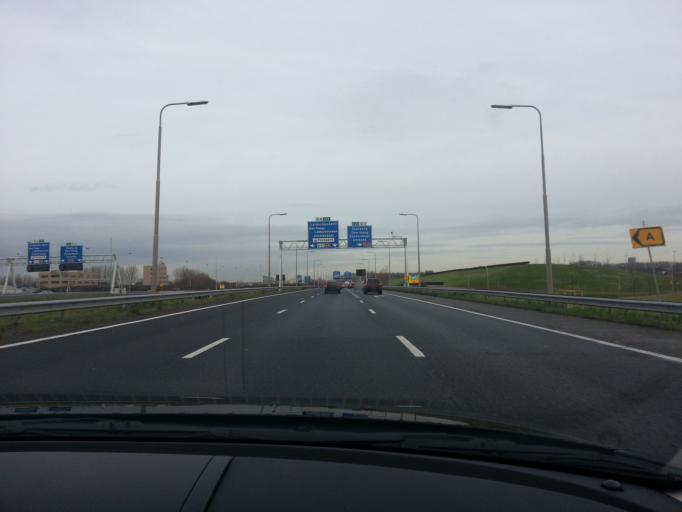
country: NL
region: South Holland
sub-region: Gemeente Den Haag
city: Ypenburg
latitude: 52.0455
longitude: 4.3558
